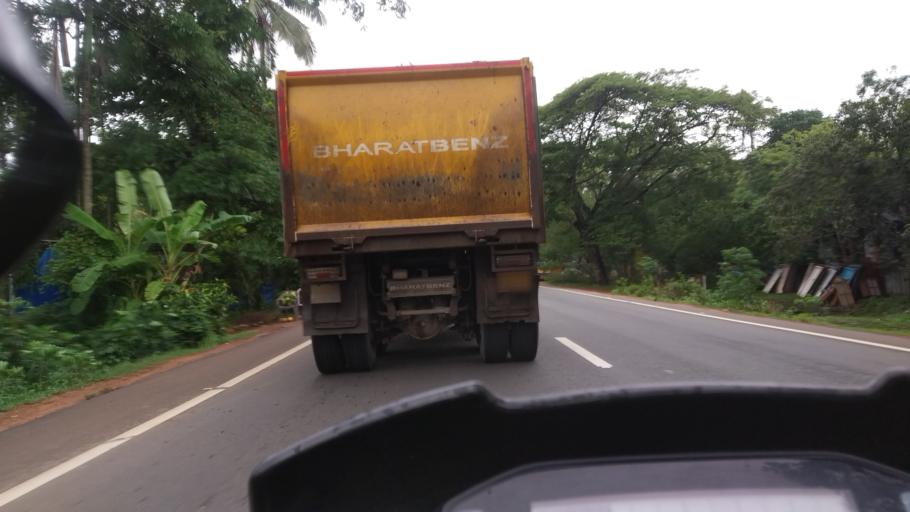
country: IN
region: Kerala
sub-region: Alappuzha
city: Shertallai
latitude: 9.6040
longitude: 76.3289
